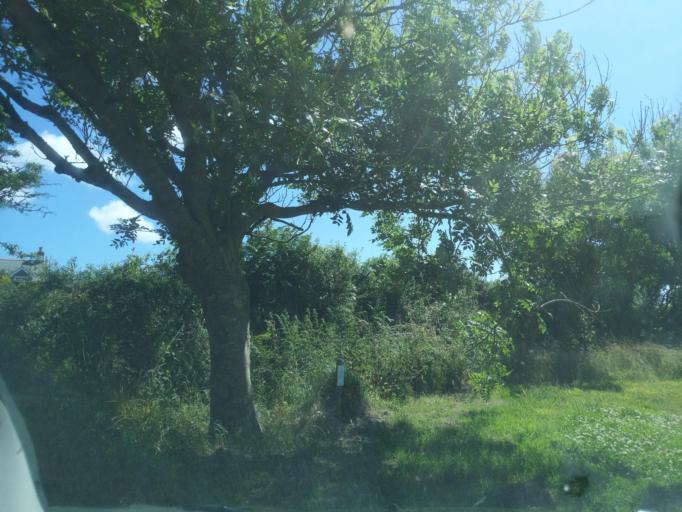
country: GB
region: England
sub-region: Cornwall
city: St. Buryan
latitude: 50.0562
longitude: -5.6622
